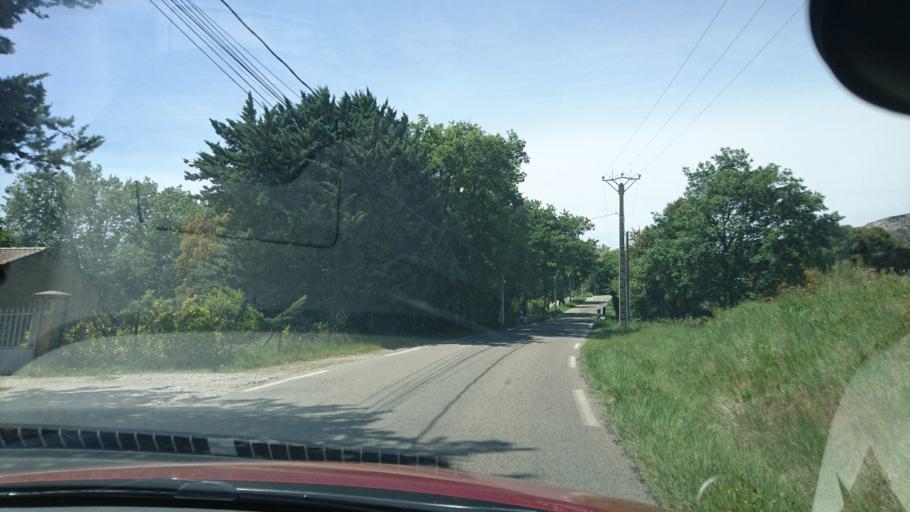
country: FR
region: Provence-Alpes-Cote d'Azur
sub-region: Departement du Vaucluse
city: Bedoin
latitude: 44.1305
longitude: 5.1727
